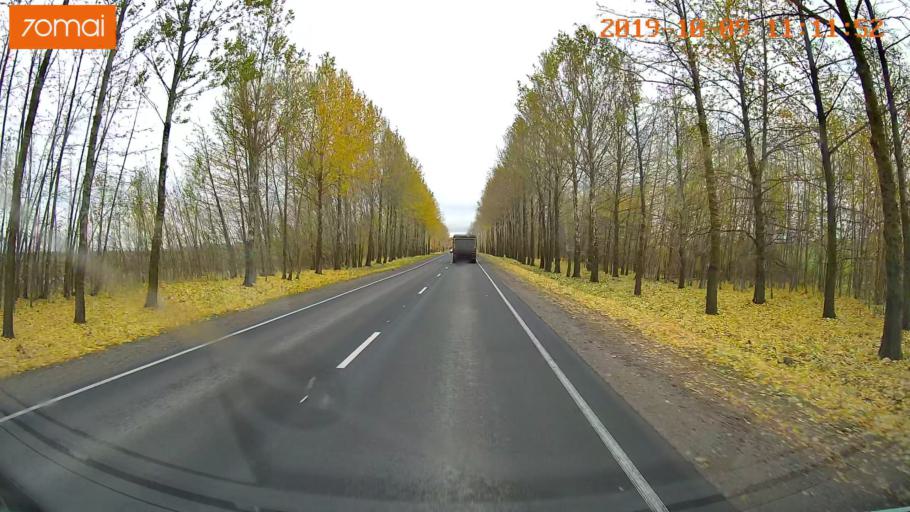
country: RU
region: Vologda
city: Vologda
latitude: 59.1723
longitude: 39.8246
